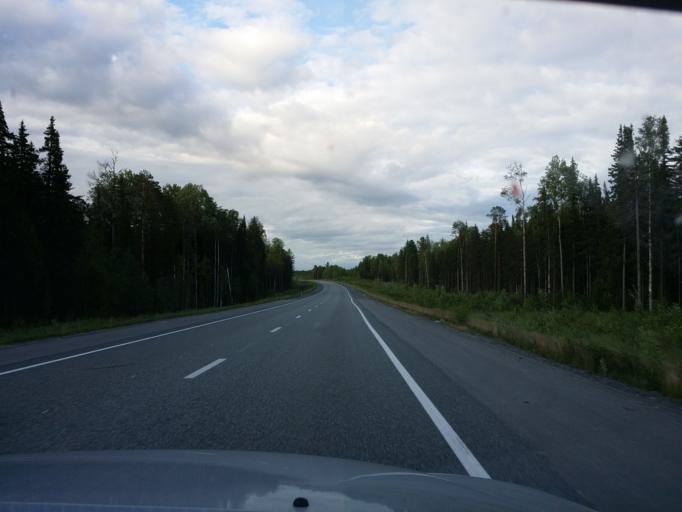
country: RU
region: Khanty-Mansiyskiy Avtonomnyy Okrug
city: Pyt-Yakh
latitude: 60.7025
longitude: 72.5305
